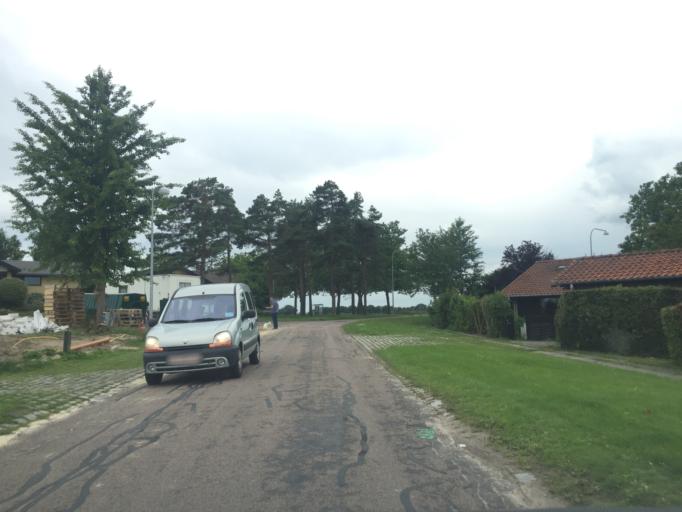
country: DK
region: Capital Region
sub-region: Lyngby-Tarbaek Kommune
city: Kongens Lyngby
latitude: 55.7838
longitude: 12.5428
